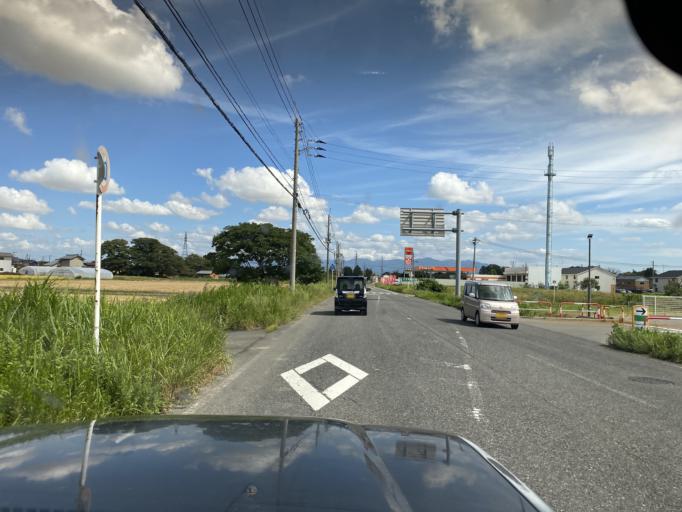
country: JP
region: Niigata
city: Niitsu-honcho
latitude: 37.8151
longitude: 139.1097
